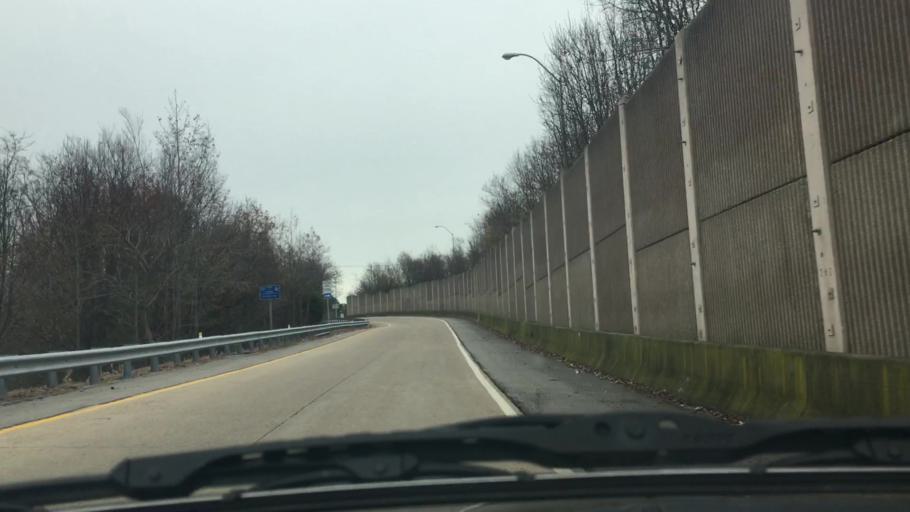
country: US
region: Virginia
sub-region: City of Portsmouth
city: Portsmouth Heights
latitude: 36.8693
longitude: -76.4032
